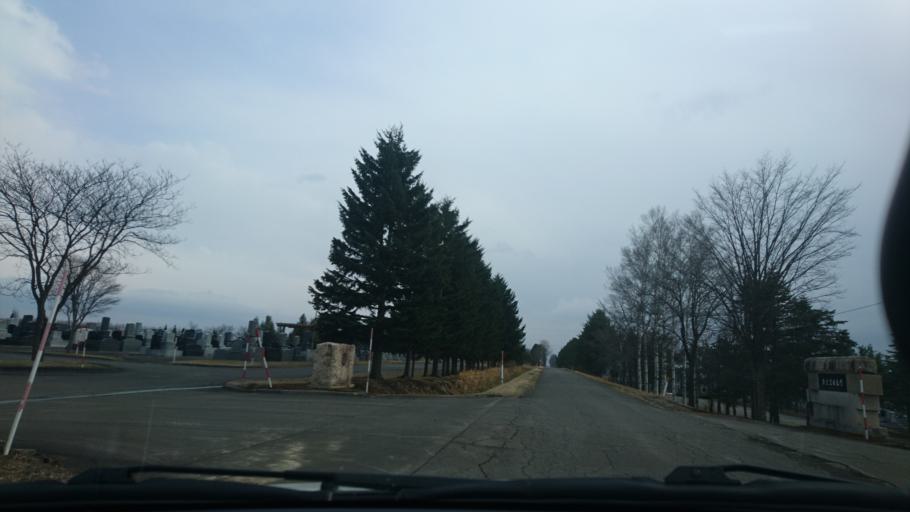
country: JP
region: Hokkaido
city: Otofuke
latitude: 43.0224
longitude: 143.2125
